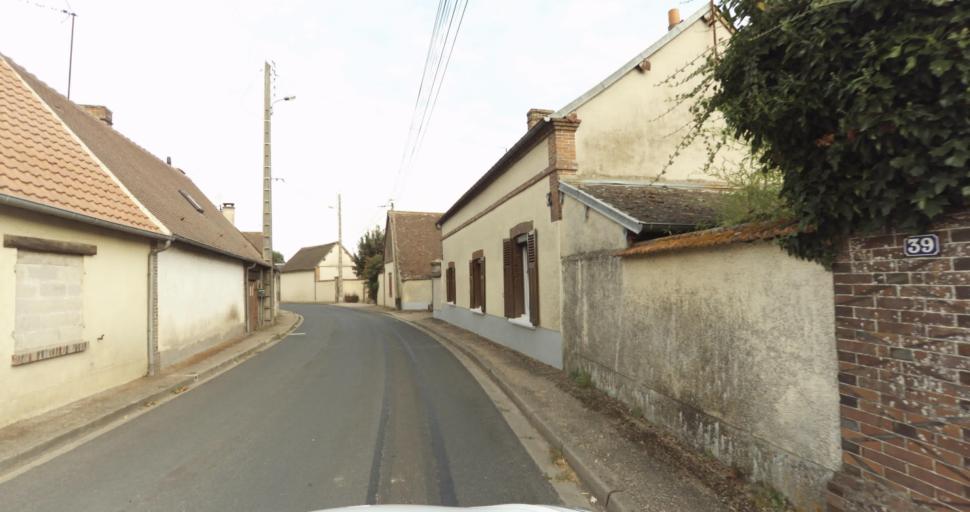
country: FR
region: Haute-Normandie
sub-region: Departement de l'Eure
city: Saint-Germain-sur-Avre
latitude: 48.8177
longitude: 1.2860
